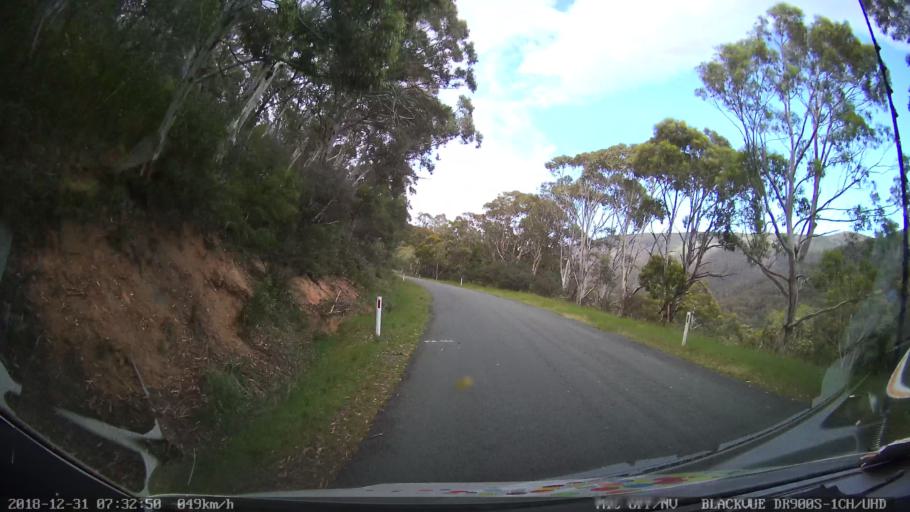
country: AU
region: New South Wales
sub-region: Snowy River
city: Jindabyne
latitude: -36.3302
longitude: 148.4619
